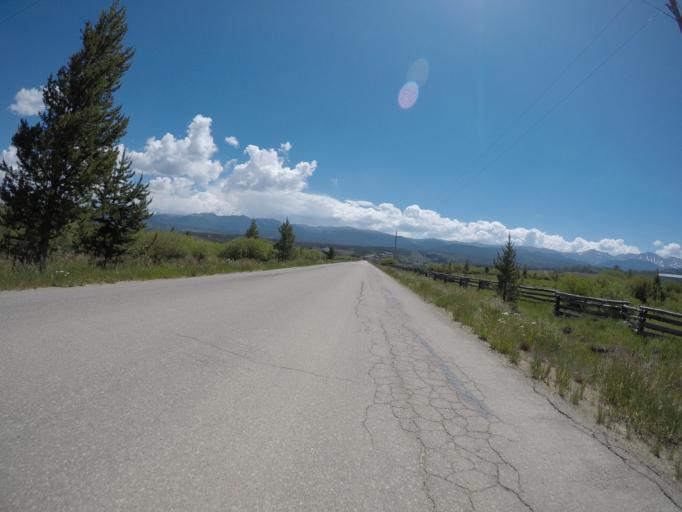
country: US
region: Colorado
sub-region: Grand County
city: Fraser
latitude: 39.9447
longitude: -105.8282
